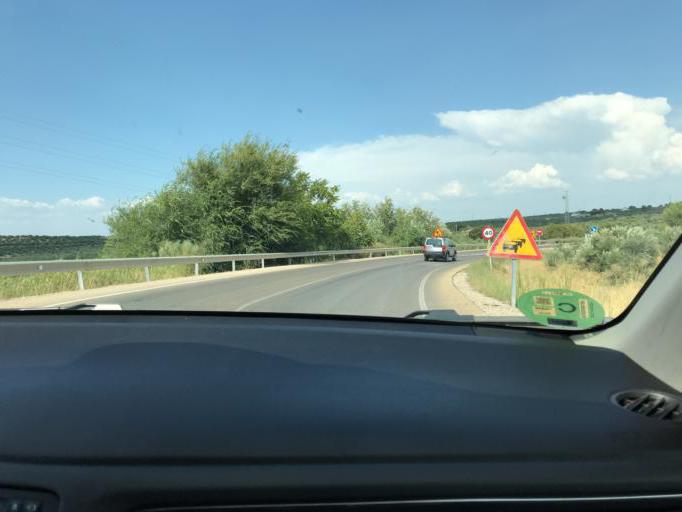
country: ES
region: Andalusia
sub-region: Provincia de Jaen
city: Ubeda
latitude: 38.0255
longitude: -3.3823
